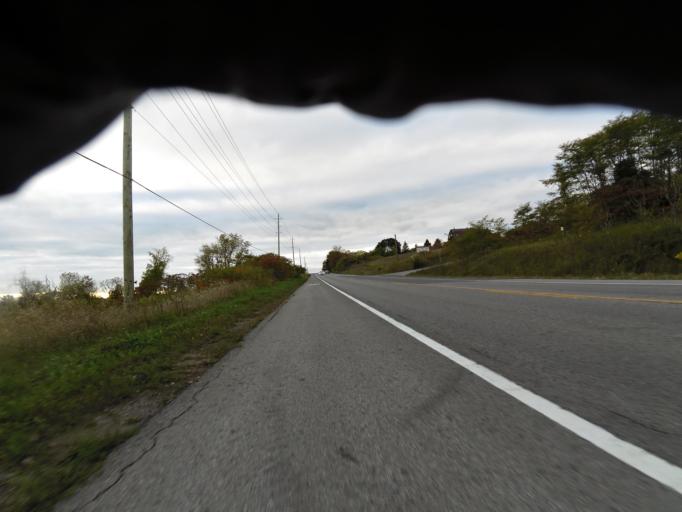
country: CA
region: Ontario
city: Cobourg
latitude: 44.0136
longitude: -77.8535
